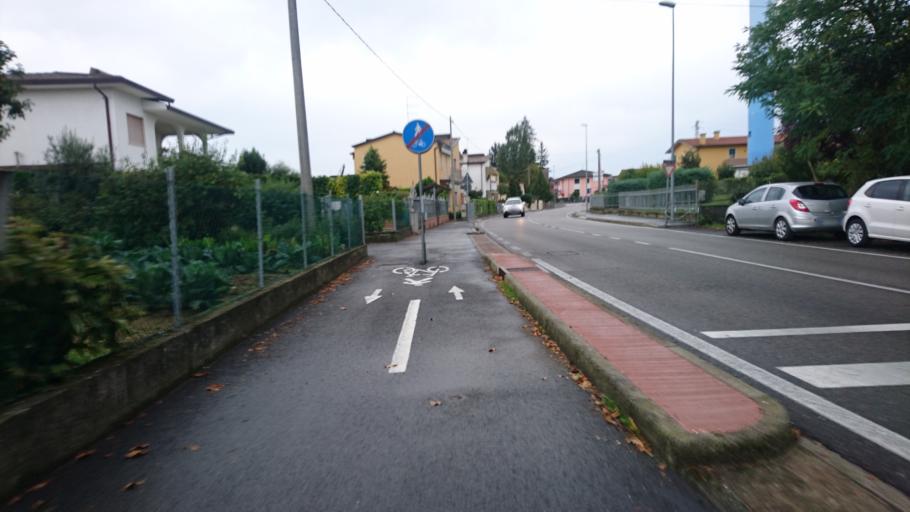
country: IT
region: Veneto
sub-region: Provincia di Padova
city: Veggiano
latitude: 45.4496
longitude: 11.7098
